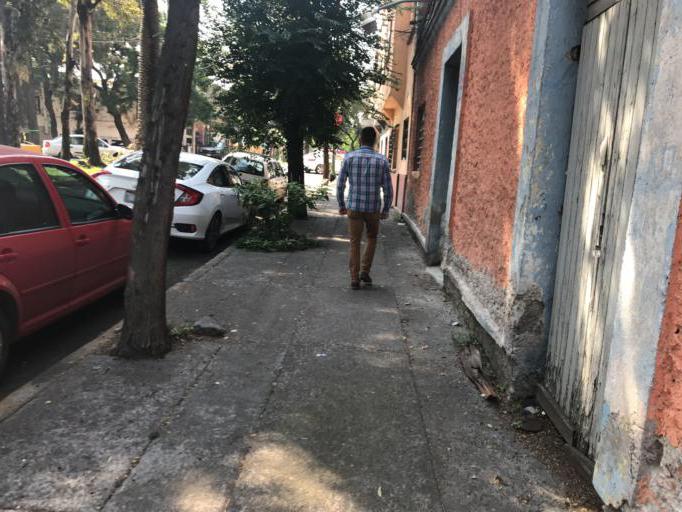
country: MX
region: Mexico
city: Colonia Lindavista
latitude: 19.4696
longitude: -99.1249
